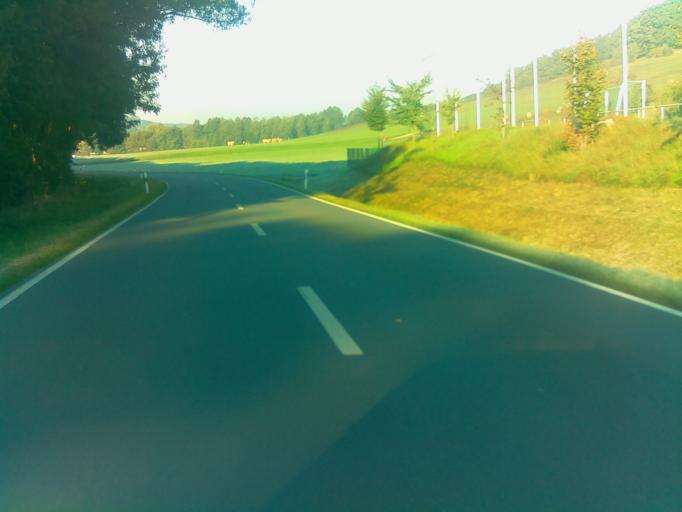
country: DE
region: Thuringia
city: Ottendorf
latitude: 50.8264
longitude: 11.8153
